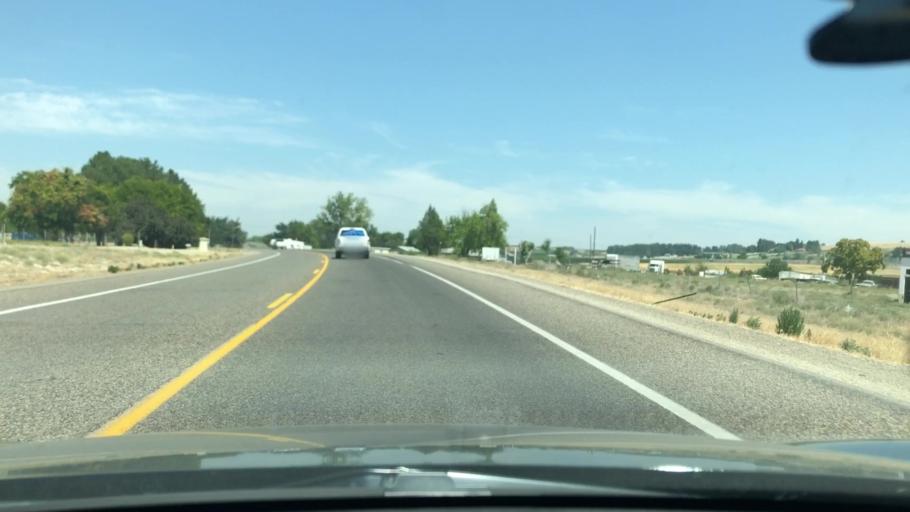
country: US
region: Idaho
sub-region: Owyhee County
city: Homedale
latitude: 43.6250
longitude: -116.9142
